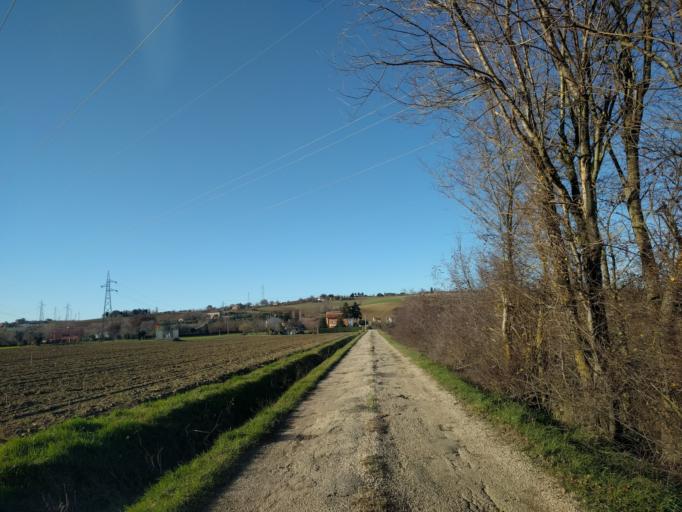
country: IT
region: The Marches
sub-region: Provincia di Pesaro e Urbino
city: Cuccurano
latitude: 43.7848
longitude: 12.9506
